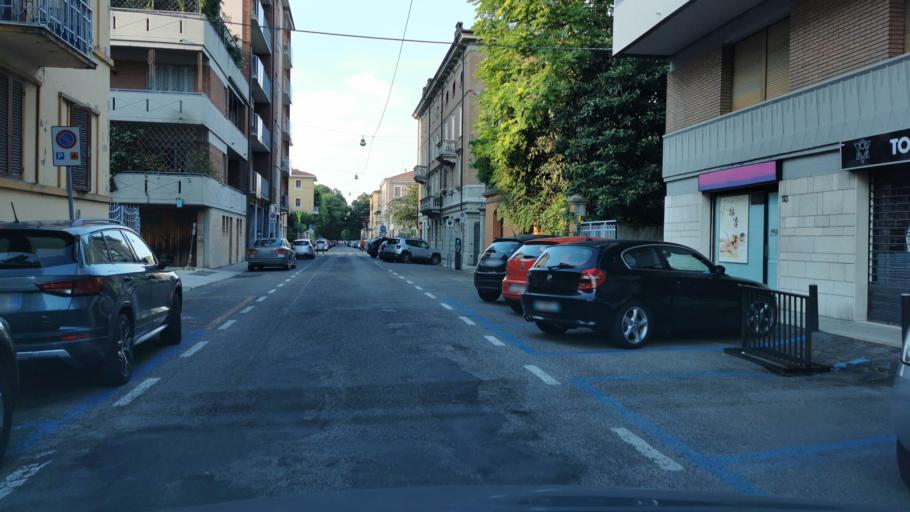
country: IT
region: Emilia-Romagna
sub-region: Provincia di Modena
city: Modena
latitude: 44.6392
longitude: 10.9296
